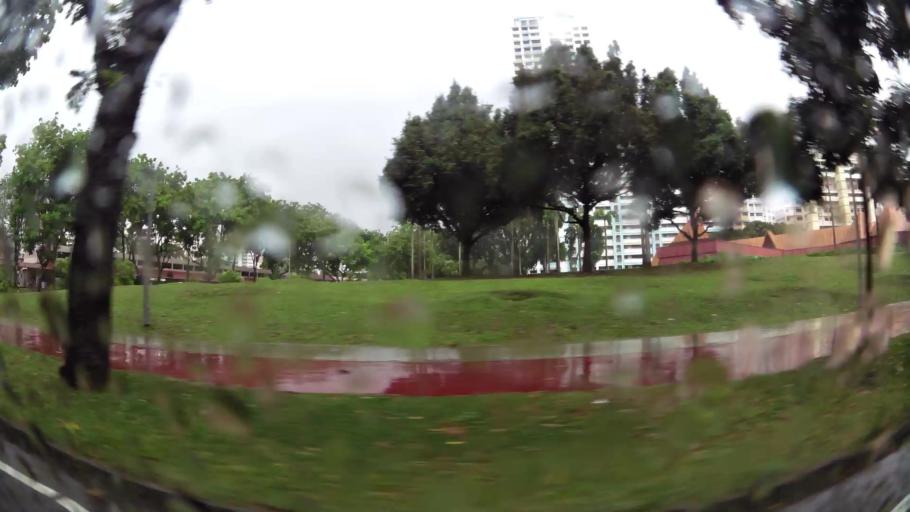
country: SG
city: Singapore
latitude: 1.3630
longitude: 103.8492
